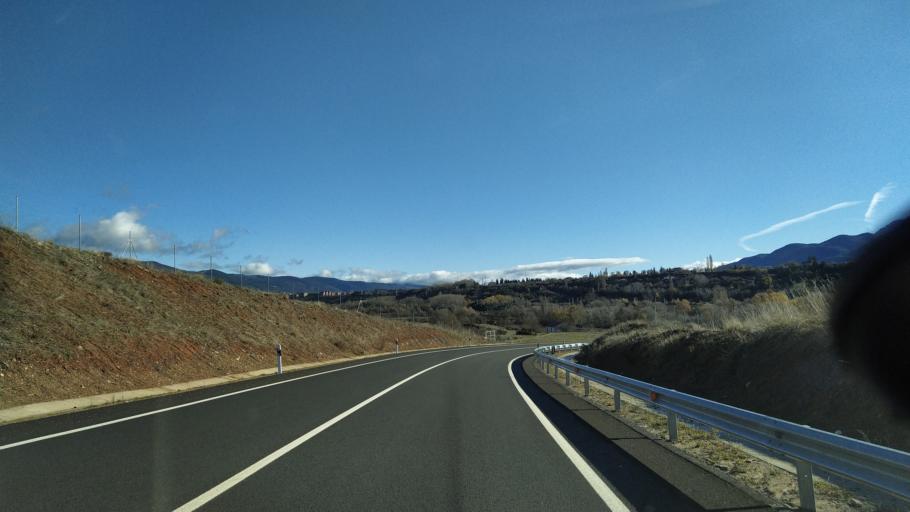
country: ES
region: Aragon
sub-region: Provincia de Huesca
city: Jaca
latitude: 42.5639
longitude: -0.5965
